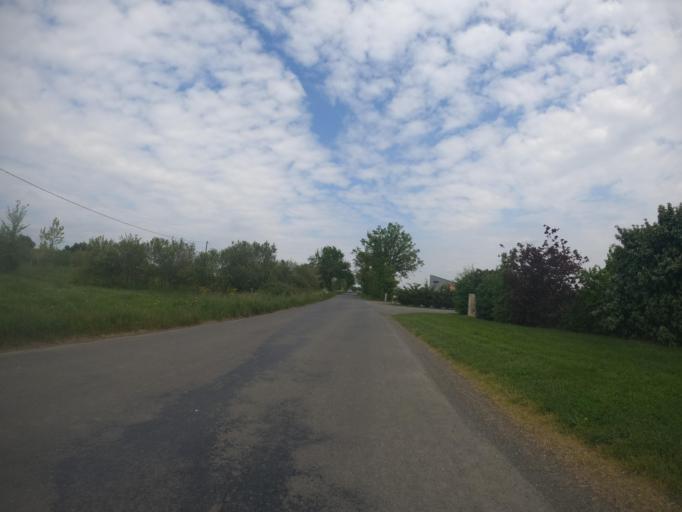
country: FR
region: Poitou-Charentes
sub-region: Departement des Deux-Sevres
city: Saint-Varent
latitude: 46.8765
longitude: -0.2793
